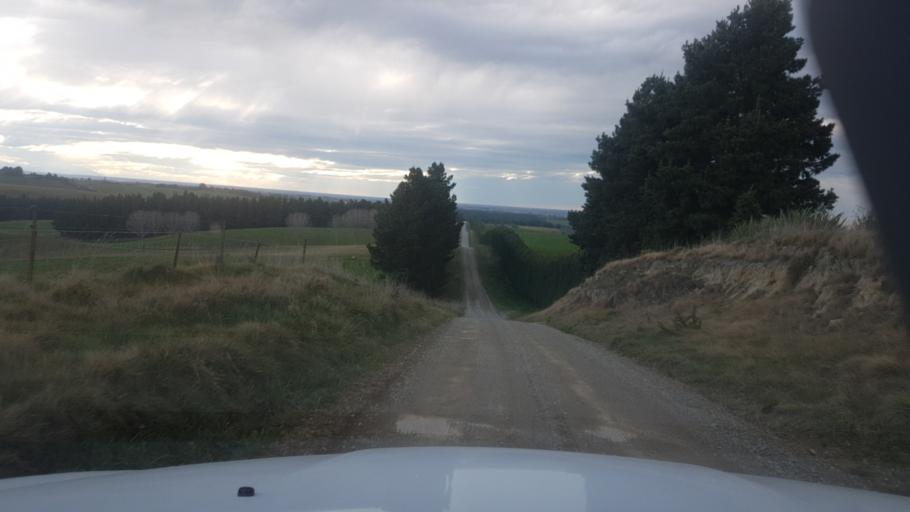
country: NZ
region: Canterbury
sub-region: Timaru District
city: Pleasant Point
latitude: -44.3440
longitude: 171.1384
